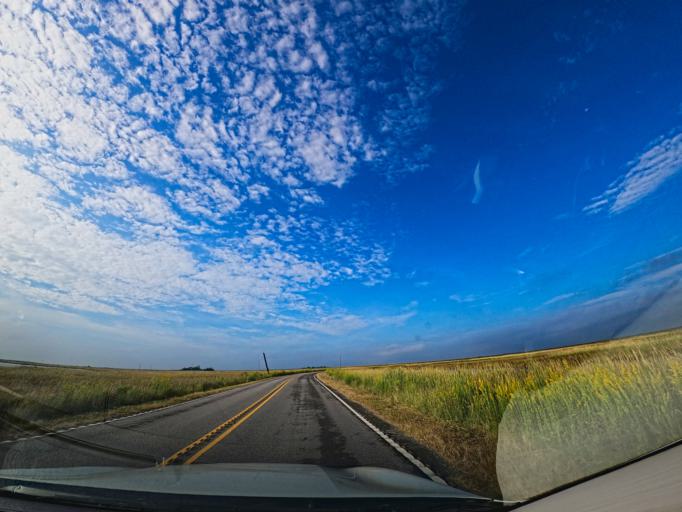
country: US
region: Louisiana
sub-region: Terrebonne Parish
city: Dulac
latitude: 29.3056
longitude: -90.6624
